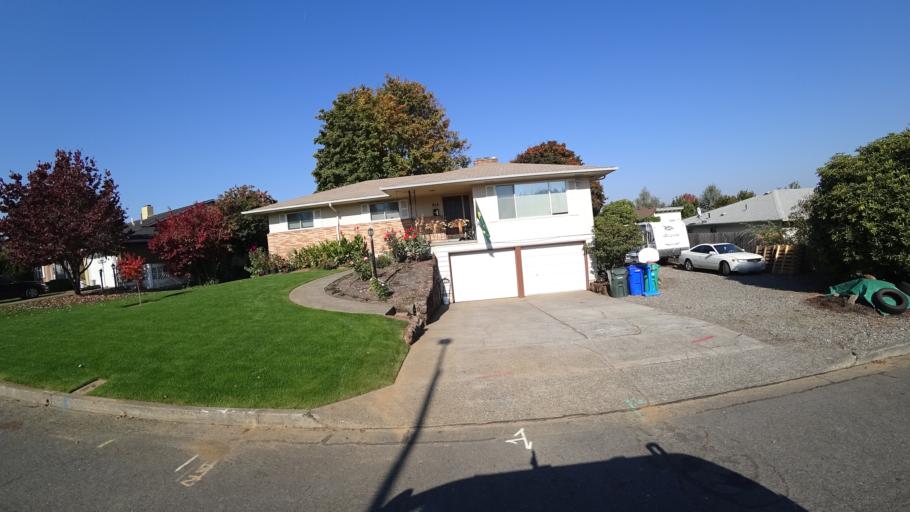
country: US
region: Oregon
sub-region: Multnomah County
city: Gresham
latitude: 45.5005
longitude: -122.4412
